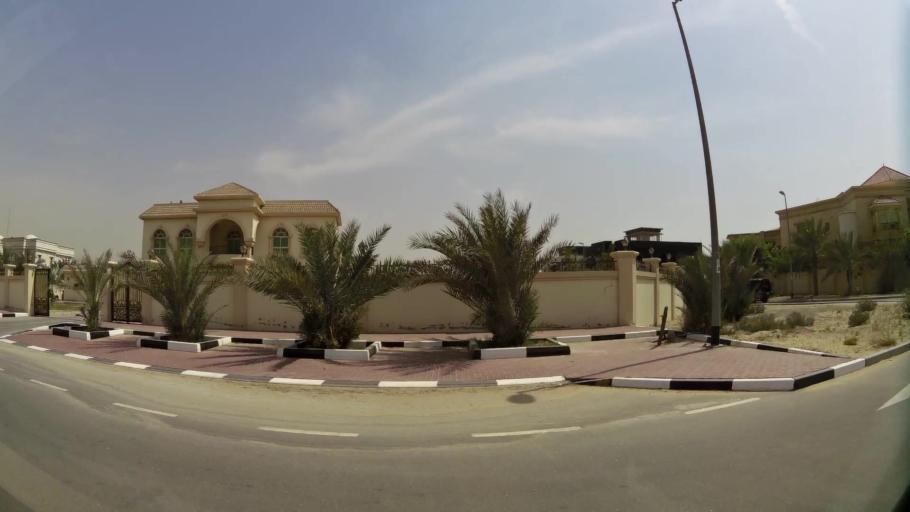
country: AE
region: Ash Shariqah
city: Sharjah
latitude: 25.2570
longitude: 55.4843
